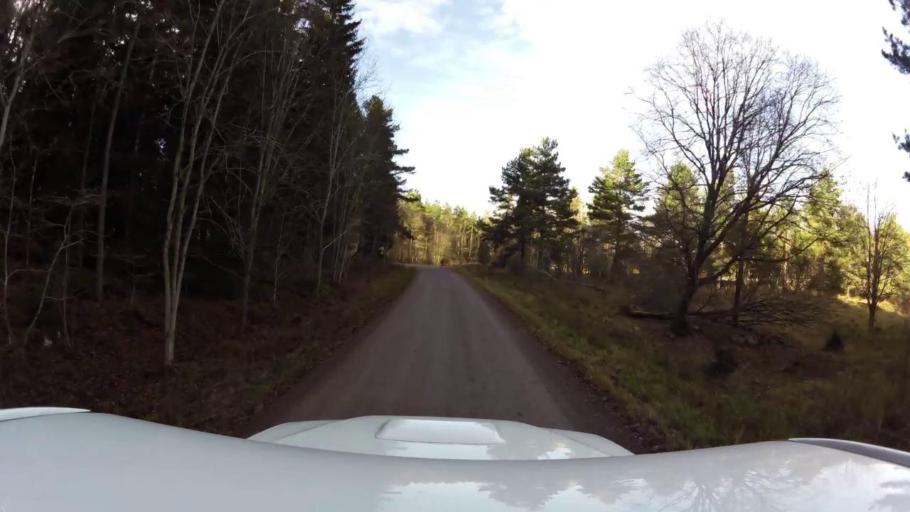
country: SE
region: OEstergoetland
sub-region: Linkopings Kommun
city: Linkoping
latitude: 58.3602
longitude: 15.6016
